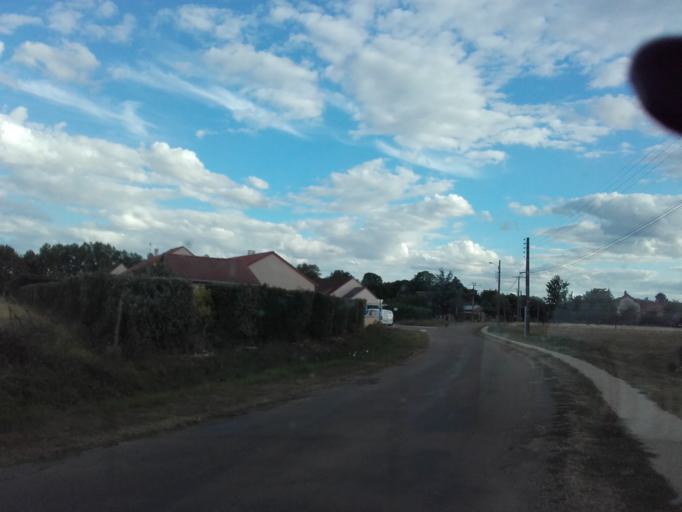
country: FR
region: Bourgogne
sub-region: Departement de Saone-et-Loire
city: Demigny
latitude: 46.9426
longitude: 4.8211
